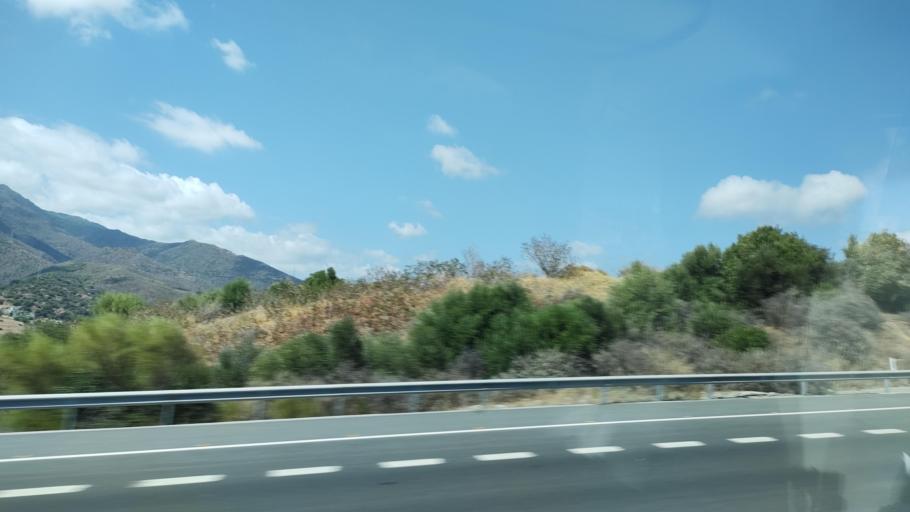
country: ES
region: Andalusia
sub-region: Provincia de Malaga
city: Estepona
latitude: 36.4339
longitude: -5.1788
